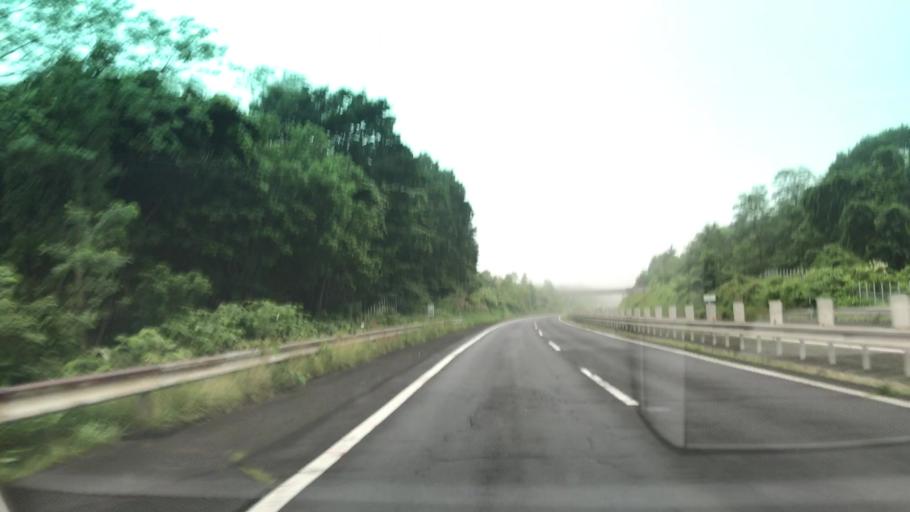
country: JP
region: Hokkaido
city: Muroran
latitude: 42.4487
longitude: 141.1576
